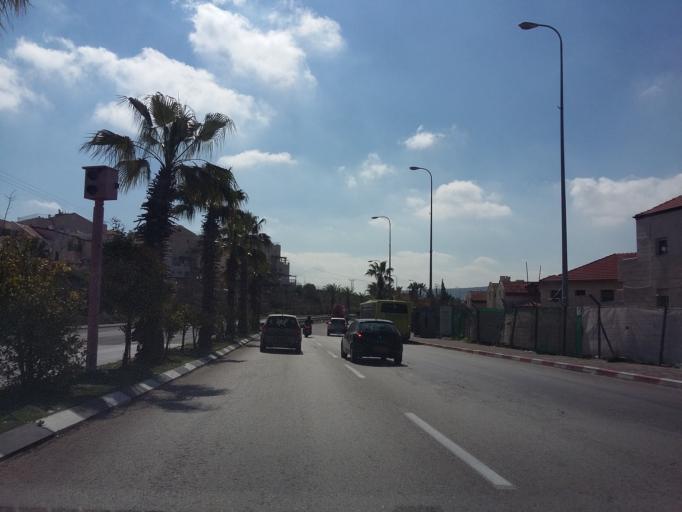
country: IL
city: Givat Zeev
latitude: 31.8625
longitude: 35.1733
